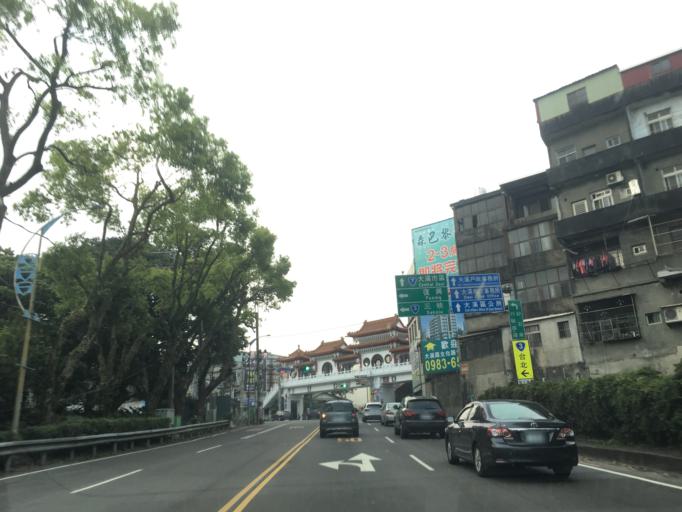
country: TW
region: Taiwan
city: Daxi
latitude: 24.8853
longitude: 121.2889
